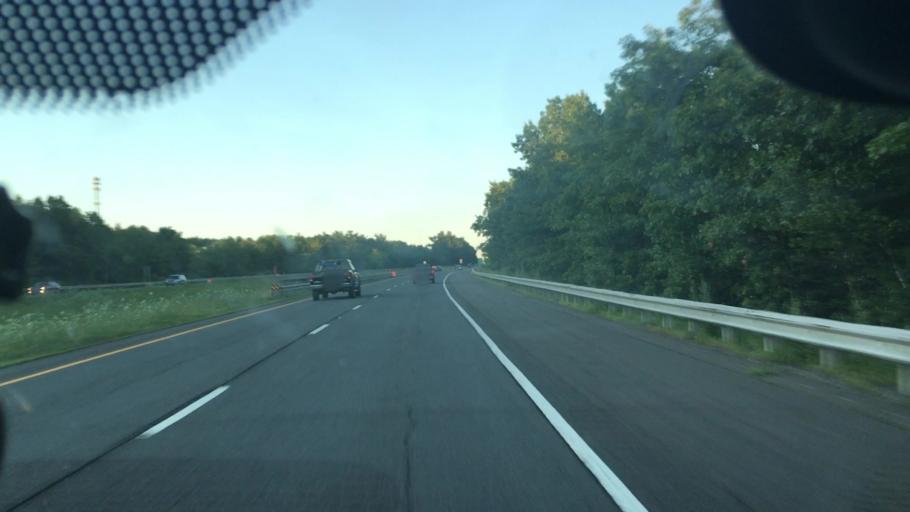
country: US
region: Massachusetts
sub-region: Franklin County
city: Bernardston
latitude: 42.6470
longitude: -72.5640
